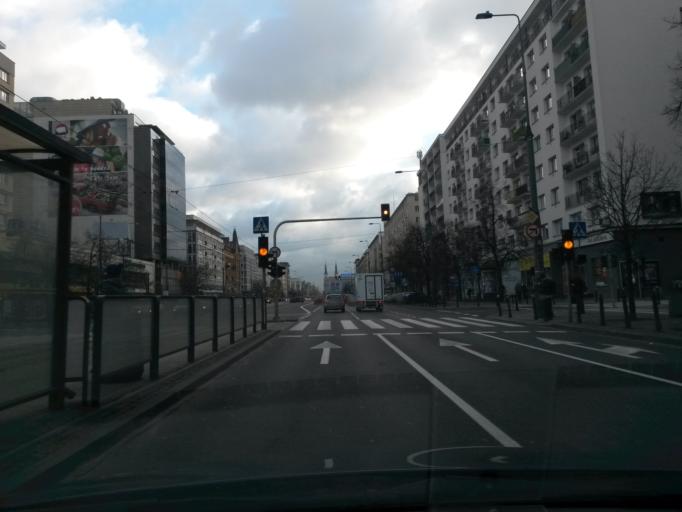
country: PL
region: Masovian Voivodeship
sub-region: Warszawa
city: Warsaw
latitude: 52.2274
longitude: 21.0131
